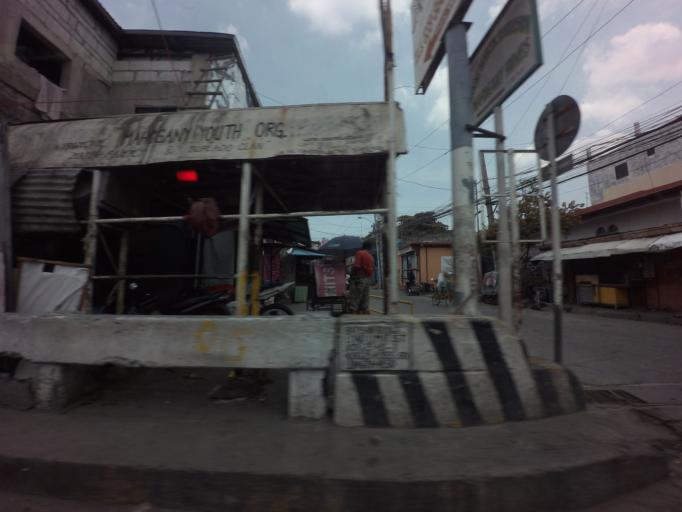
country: PH
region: Calabarzon
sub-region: Province of Rizal
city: Taguig
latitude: 14.4763
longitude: 121.0600
